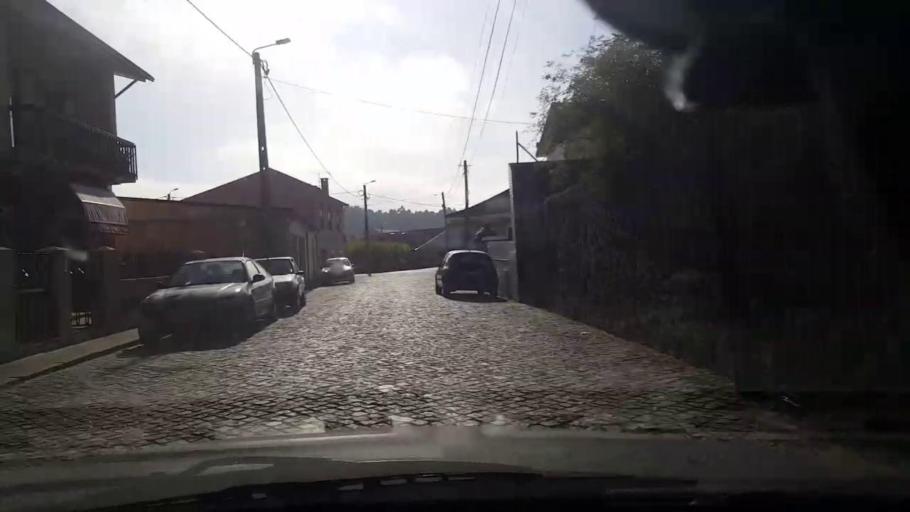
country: PT
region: Porto
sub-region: Maia
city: Gemunde
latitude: 41.2665
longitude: -8.6702
